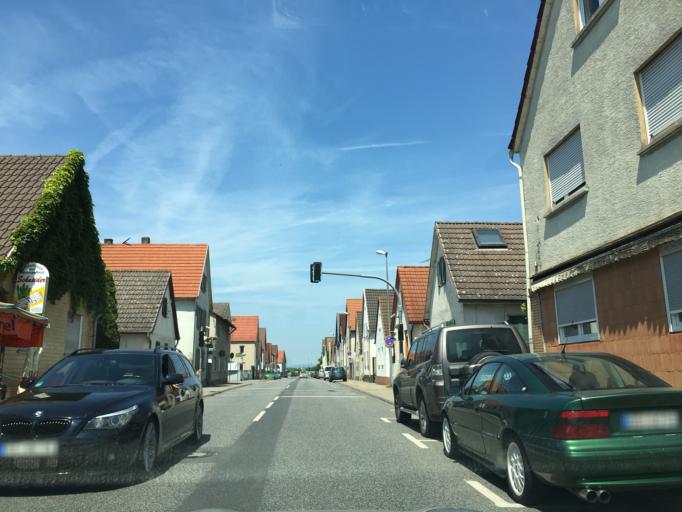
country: DE
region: Hesse
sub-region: Regierungsbezirk Darmstadt
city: Gross-Gerau
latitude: 49.8795
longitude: 8.4810
